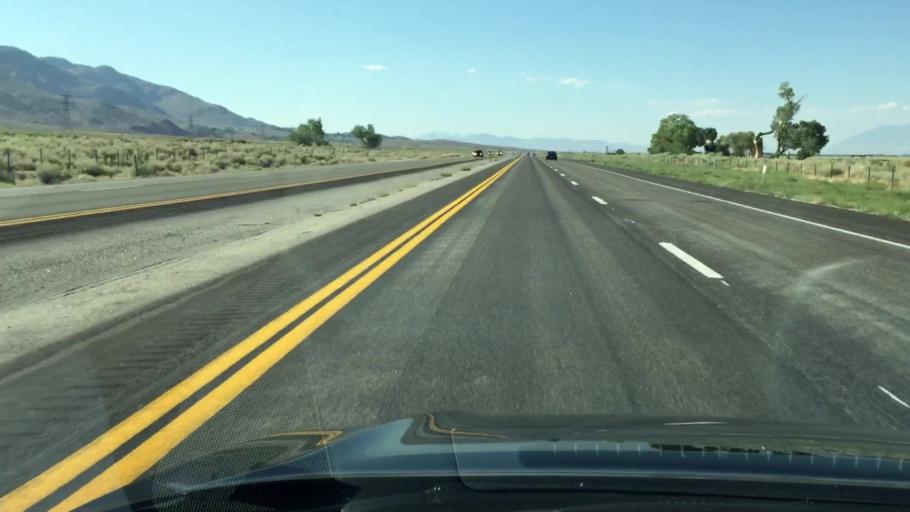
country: US
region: California
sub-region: Inyo County
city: Big Pine
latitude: 37.2420
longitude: -118.3516
